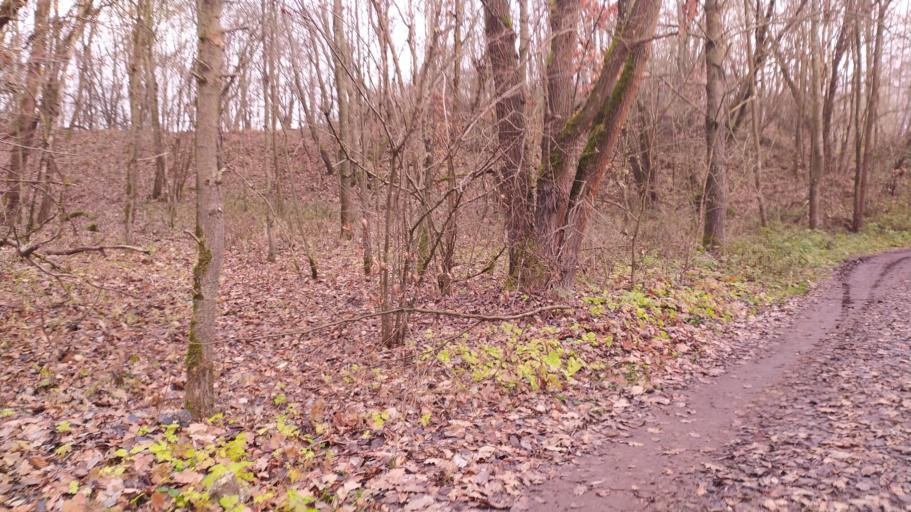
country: DE
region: Bavaria
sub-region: Upper Franconia
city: Schirnding
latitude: 50.1020
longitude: 12.2544
